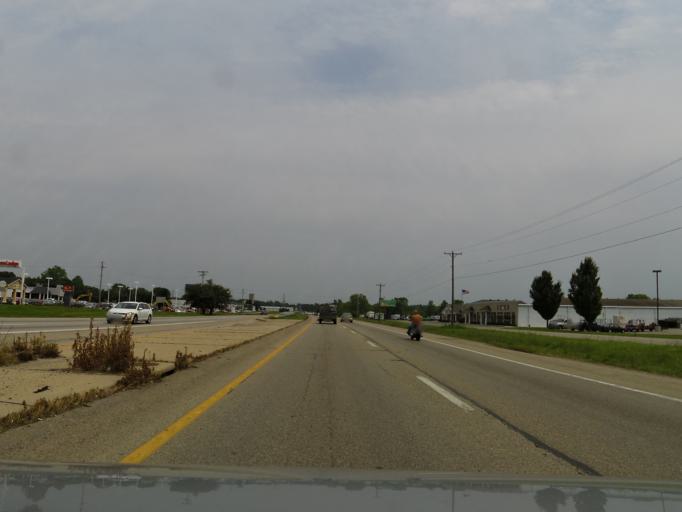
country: US
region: Ohio
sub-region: Greene County
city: Beavercreek
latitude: 39.7060
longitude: -84.0189
